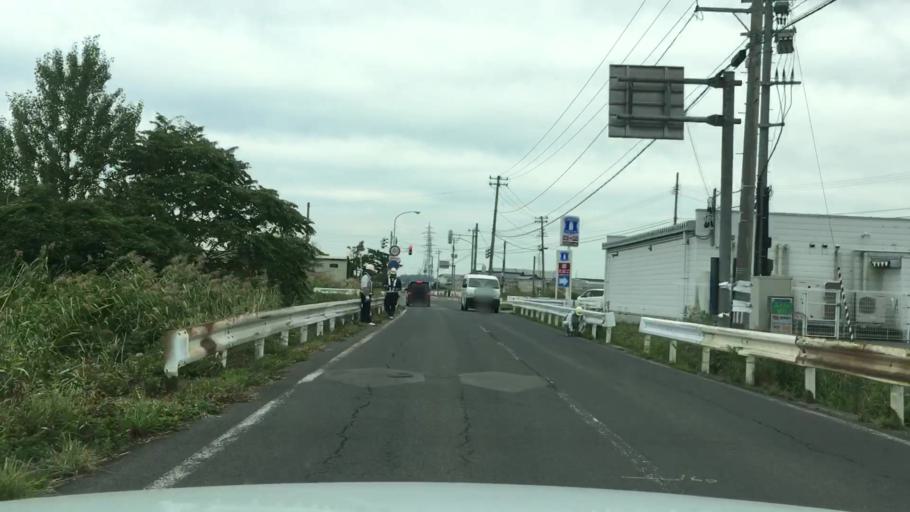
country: JP
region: Aomori
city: Hirosaki
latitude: 40.6304
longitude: 140.4526
